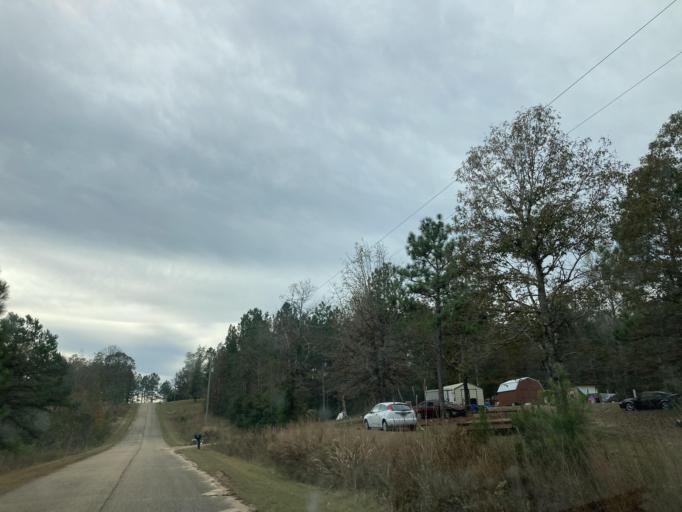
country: US
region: Mississippi
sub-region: Lamar County
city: Purvis
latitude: 31.1174
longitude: -89.4485
